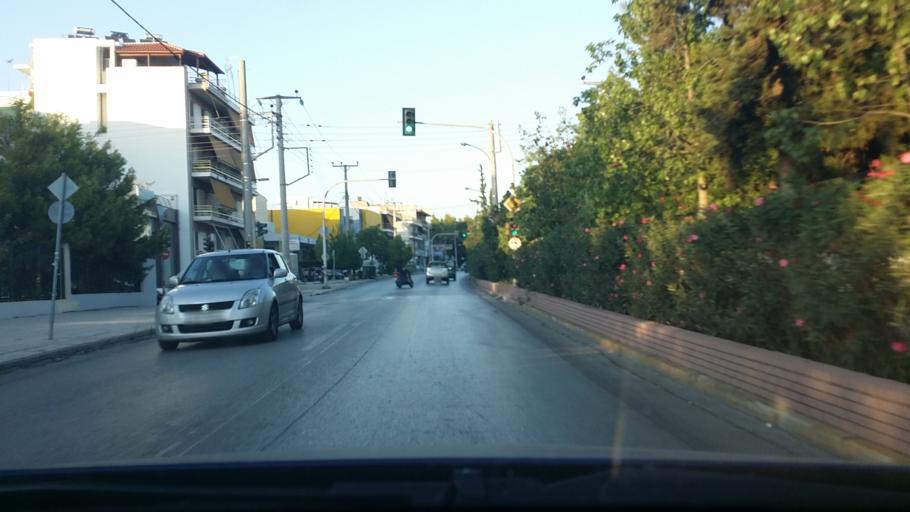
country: GR
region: Attica
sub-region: Nomarchia Athinas
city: Nea Filadelfeia
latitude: 38.0475
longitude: 23.7462
